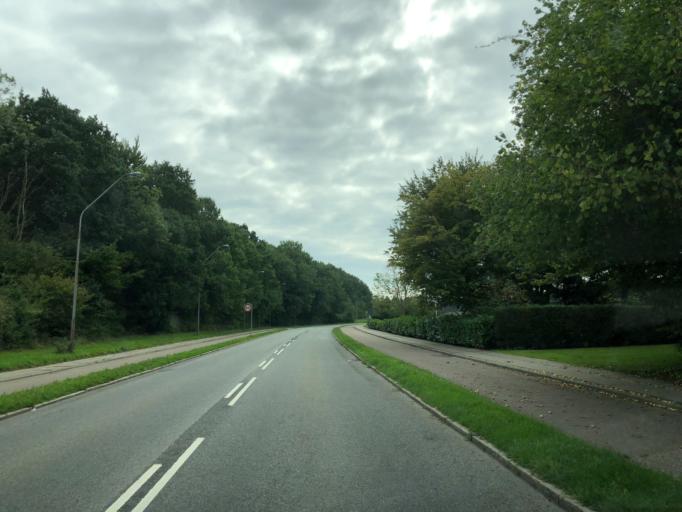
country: DK
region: South Denmark
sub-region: Sonderborg Kommune
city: Sonderborg
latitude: 54.9019
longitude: 9.8244
